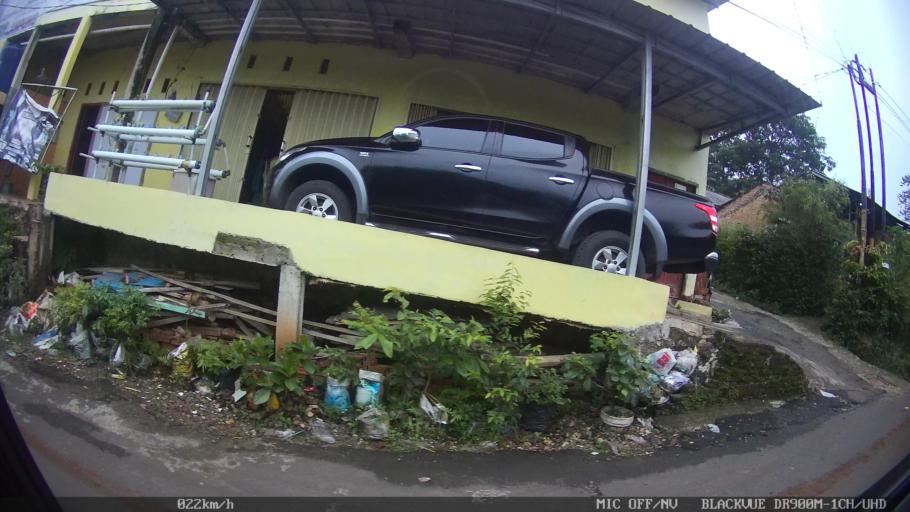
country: ID
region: Lampung
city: Kedaton
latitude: -5.4036
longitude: 105.2407
